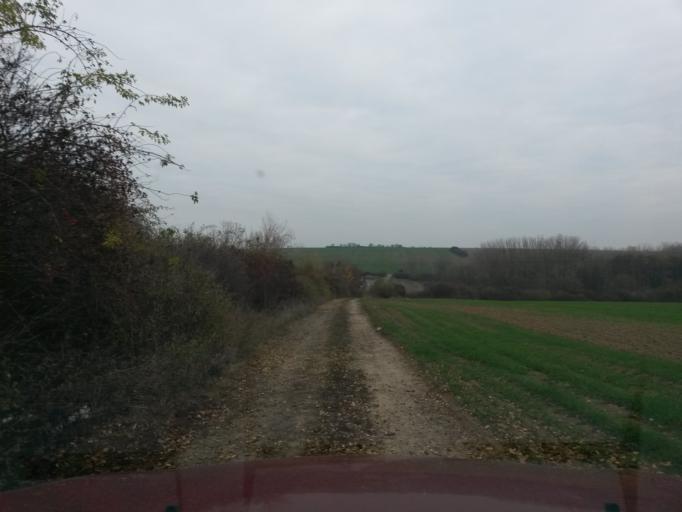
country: SK
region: Kosicky
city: Secovce
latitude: 48.6445
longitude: 21.6076
